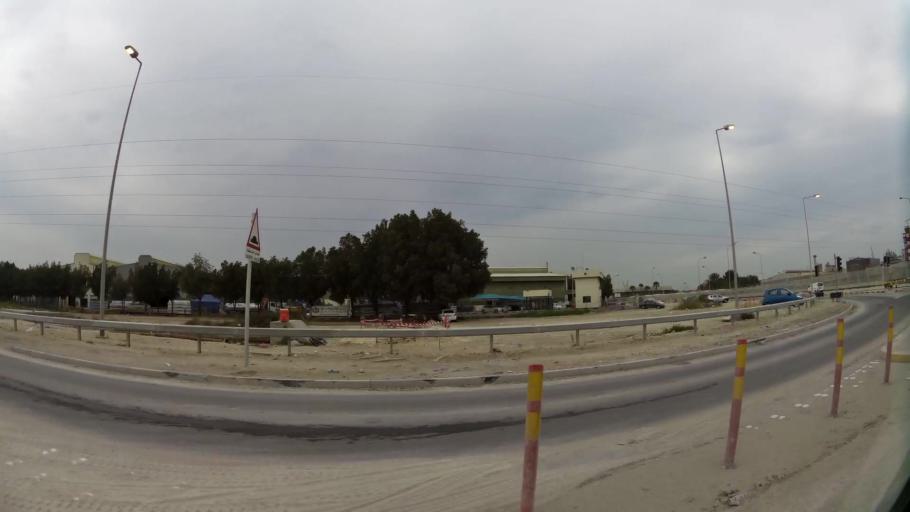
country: BH
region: Northern
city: Sitrah
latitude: 26.1803
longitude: 50.6233
